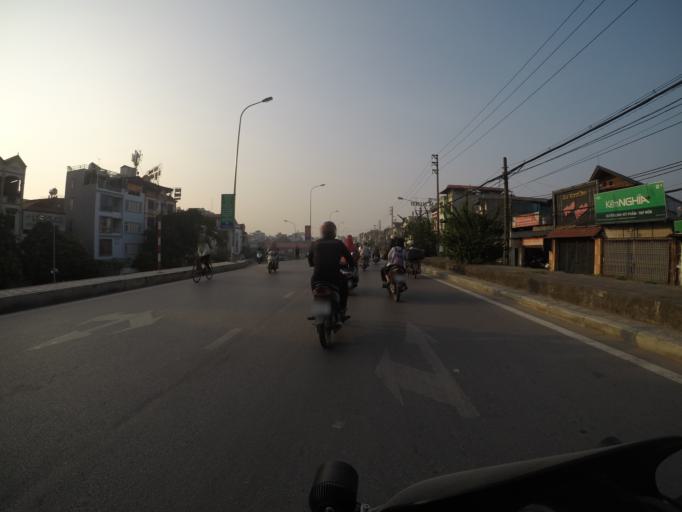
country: VN
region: Ha Noi
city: Hoan Kiem
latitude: 21.0432
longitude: 105.8654
